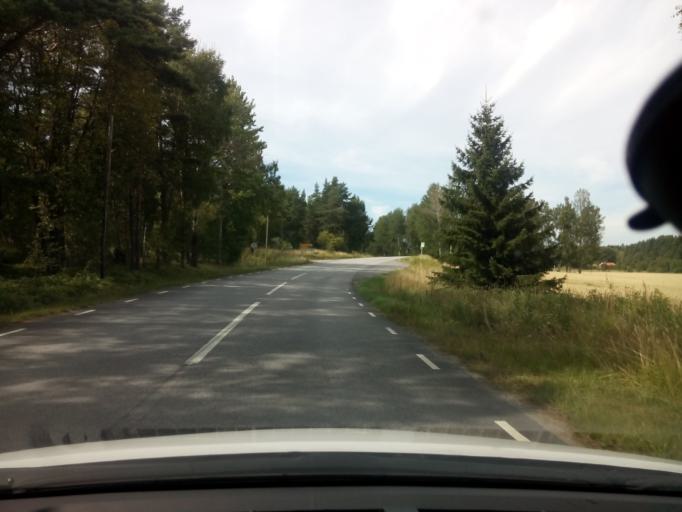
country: SE
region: Soedermanland
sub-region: Oxelosunds Kommun
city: Oxelosund
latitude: 58.7450
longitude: 17.1352
